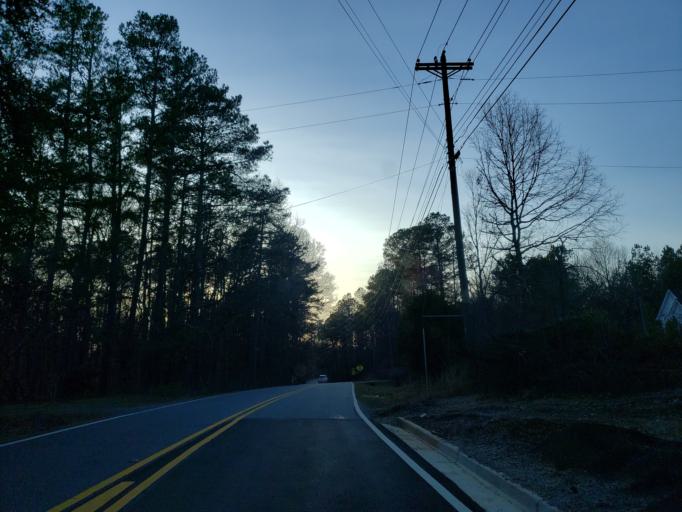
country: US
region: Georgia
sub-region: Cobb County
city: Acworth
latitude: 34.0258
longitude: -84.7313
